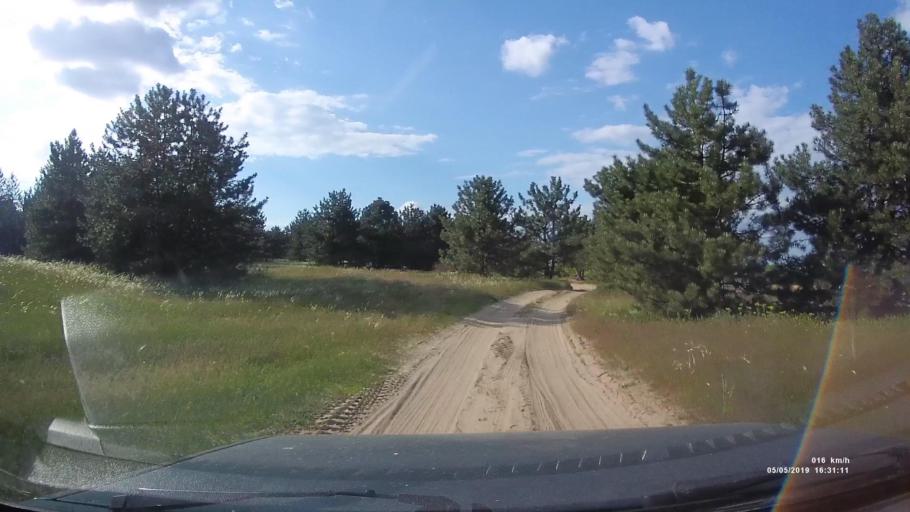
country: RU
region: Rostov
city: Ust'-Donetskiy
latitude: 47.7757
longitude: 41.0151
